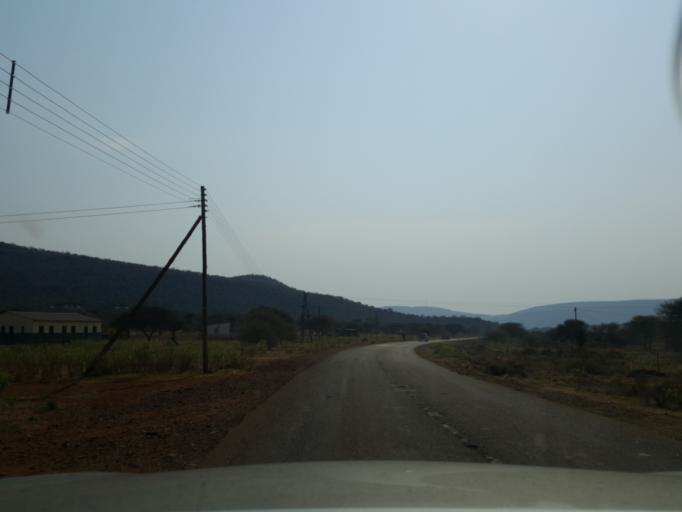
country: BW
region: South East
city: Lobatse
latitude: -25.3065
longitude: 25.8158
